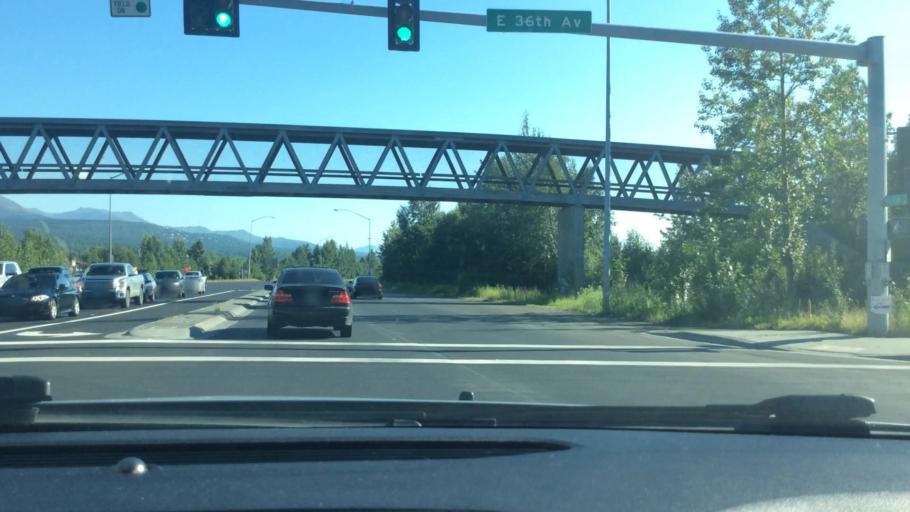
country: US
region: Alaska
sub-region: Anchorage Municipality
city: Elmendorf Air Force Base
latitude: 61.1881
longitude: -149.7333
